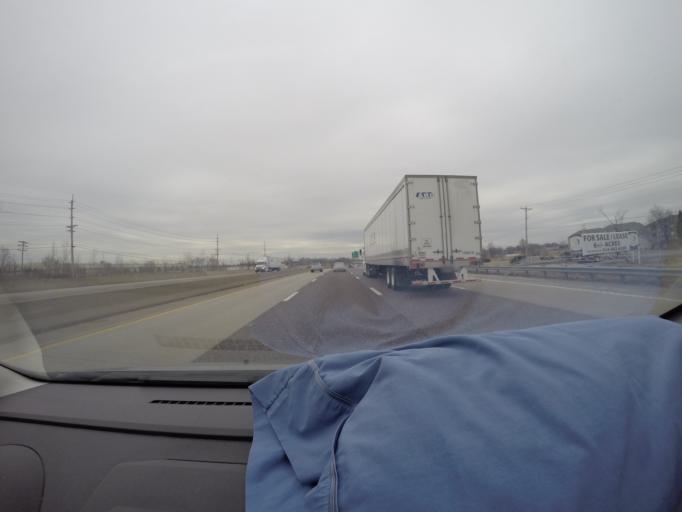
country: US
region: Missouri
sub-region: Saint Charles County
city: Saint Peters
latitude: 38.8025
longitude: -90.6586
